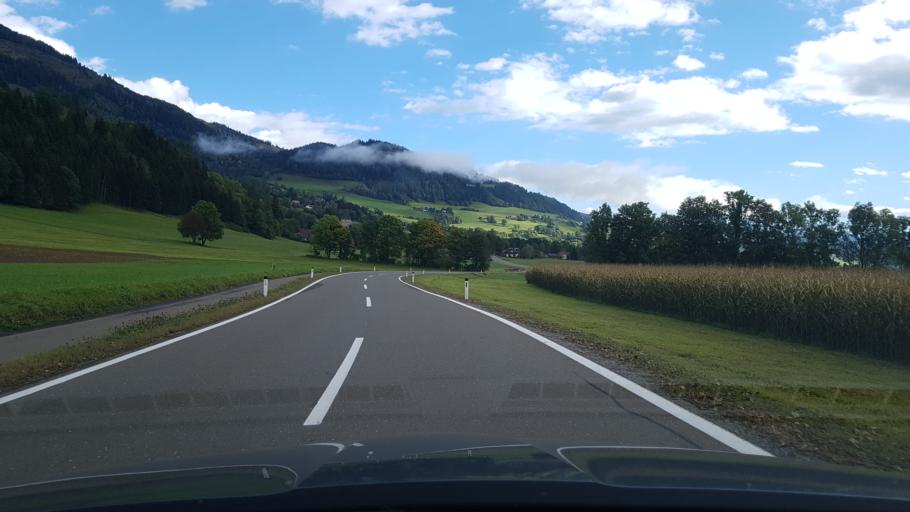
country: AT
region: Styria
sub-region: Politischer Bezirk Murau
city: Schoder
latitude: 47.1844
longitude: 14.1206
